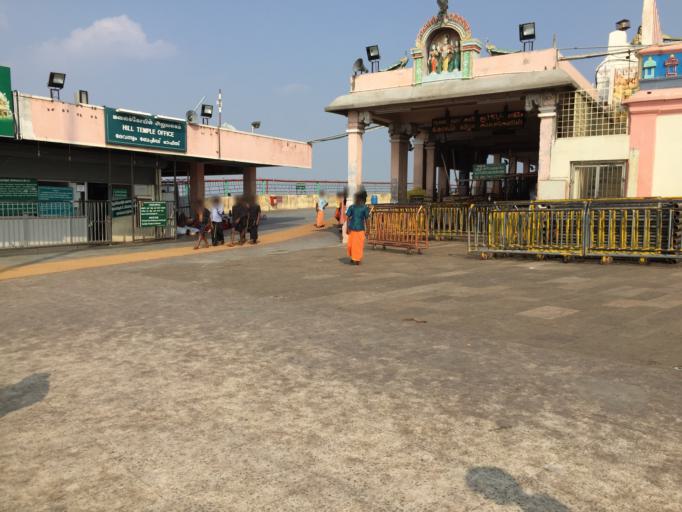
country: IN
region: Tamil Nadu
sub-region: Dindigul
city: Palani
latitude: 10.4390
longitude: 77.5196
